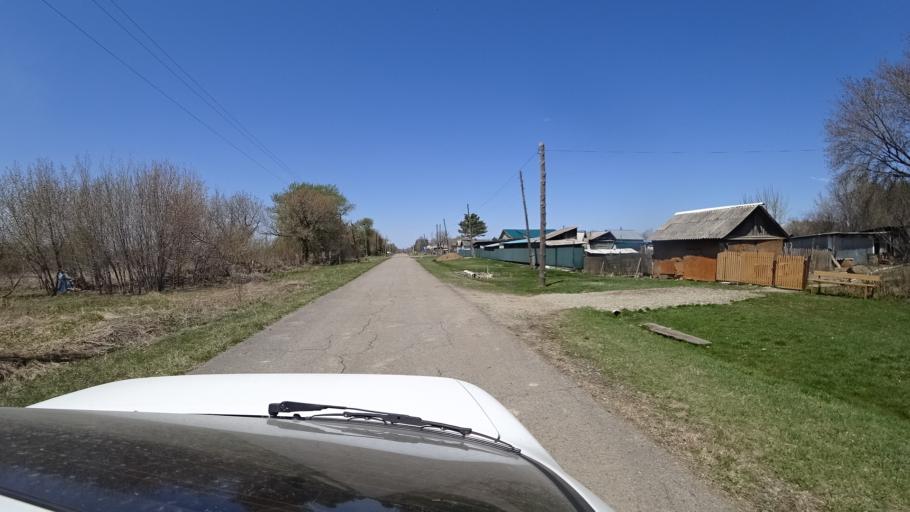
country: RU
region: Primorskiy
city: Lazo
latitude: 45.7907
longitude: 133.7678
